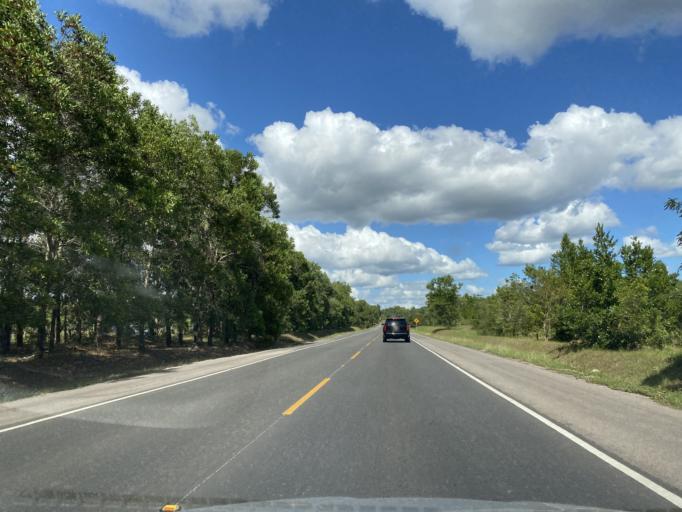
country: DO
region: Monte Plata
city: Monte Plata
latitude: 18.7549
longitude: -69.7651
